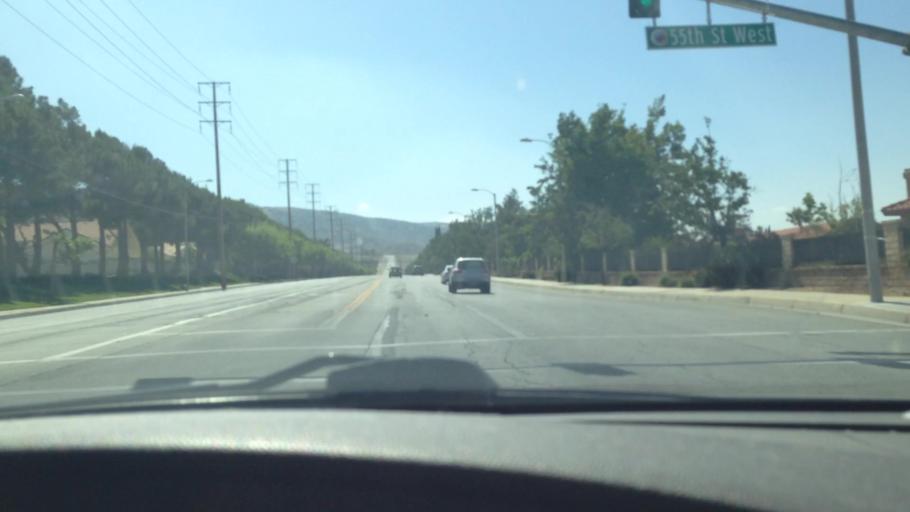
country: US
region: California
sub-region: Los Angeles County
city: Quartz Hill
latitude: 34.6309
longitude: -118.2276
